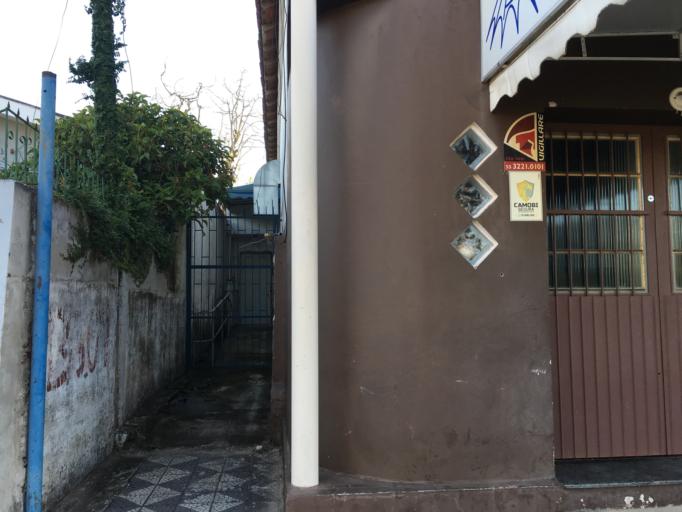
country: BR
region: Rio Grande do Sul
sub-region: Santa Maria
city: Santa Maria
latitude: -29.7003
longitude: -53.7079
